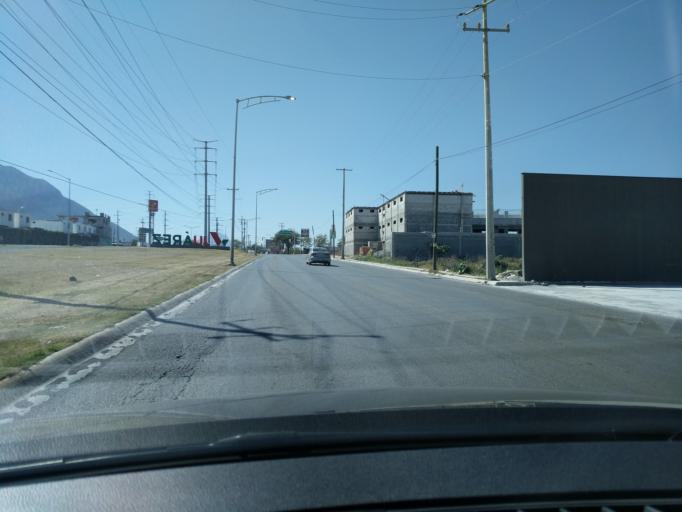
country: MX
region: Nuevo Leon
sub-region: Juarez
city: Valle de Vaquerias
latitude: 25.6393
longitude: -100.1499
